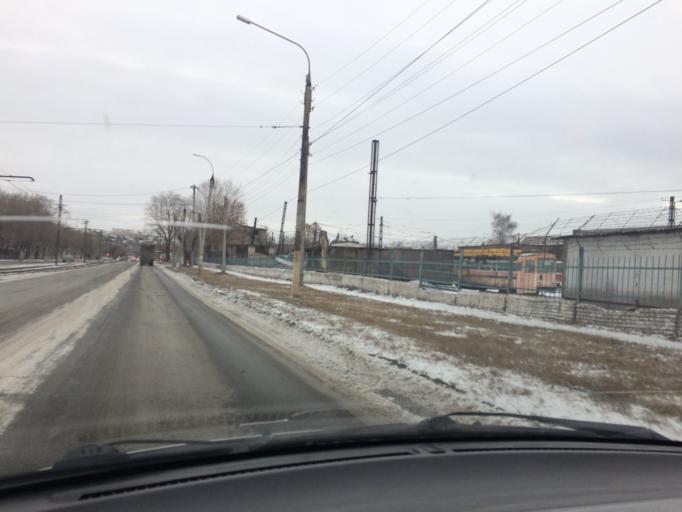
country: RU
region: Chelyabinsk
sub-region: Gorod Magnitogorsk
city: Magnitogorsk
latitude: 53.3862
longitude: 59.0778
